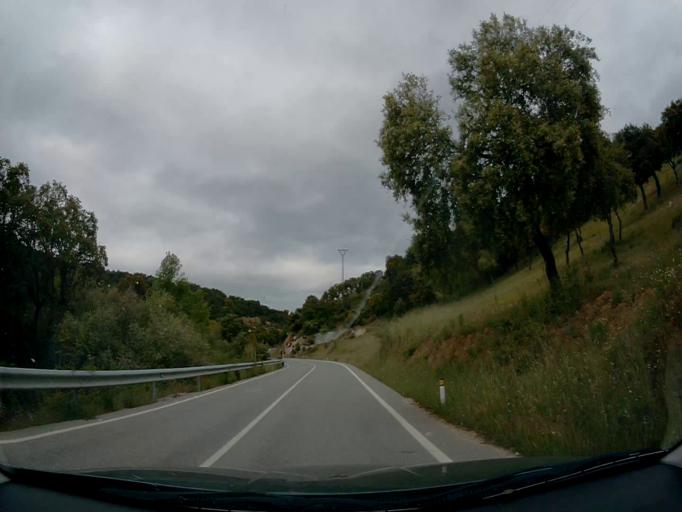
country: ES
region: Madrid
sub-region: Provincia de Madrid
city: Navalagamella
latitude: 40.4395
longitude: -4.1116
